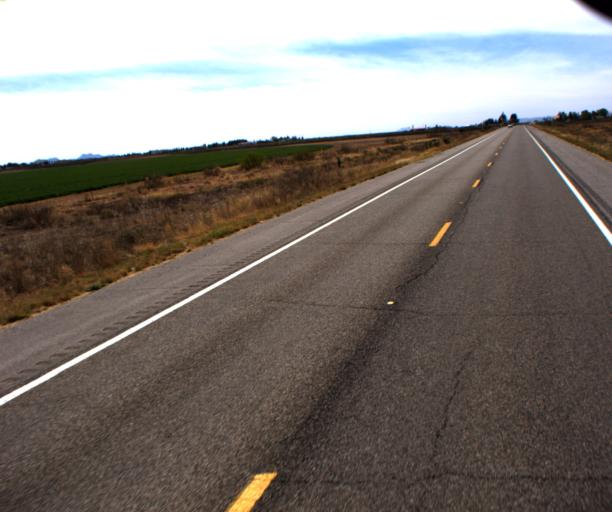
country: US
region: Arizona
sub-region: Cochise County
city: Pirtleville
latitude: 31.6100
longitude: -109.6706
